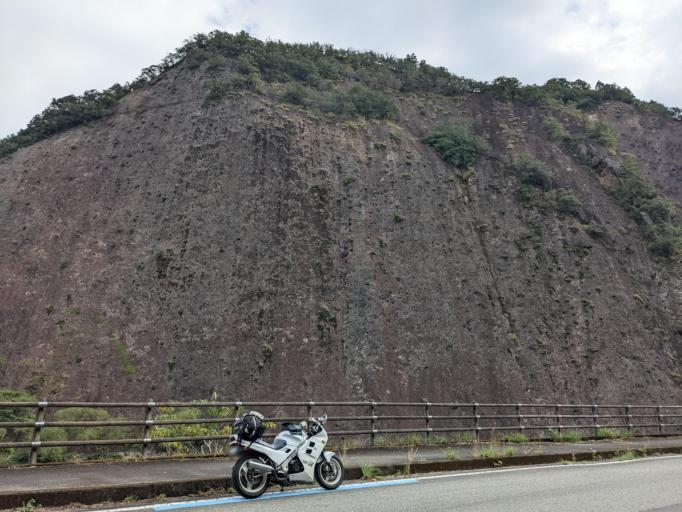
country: JP
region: Wakayama
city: Shingu
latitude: 33.5465
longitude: 135.7190
